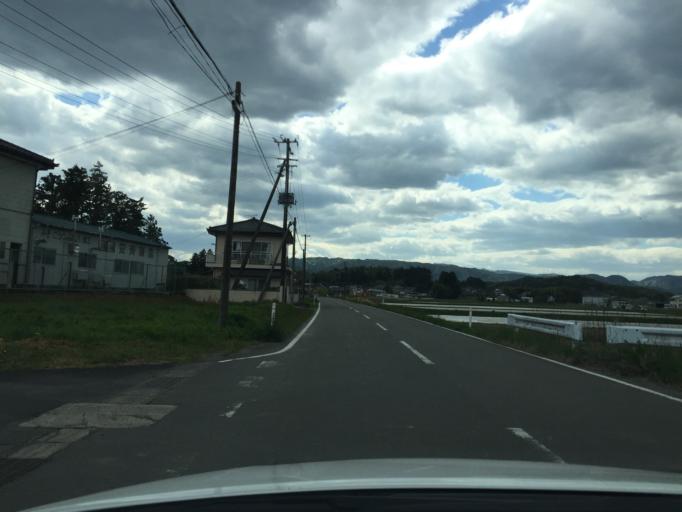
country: JP
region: Miyagi
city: Marumori
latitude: 37.7573
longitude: 140.9430
